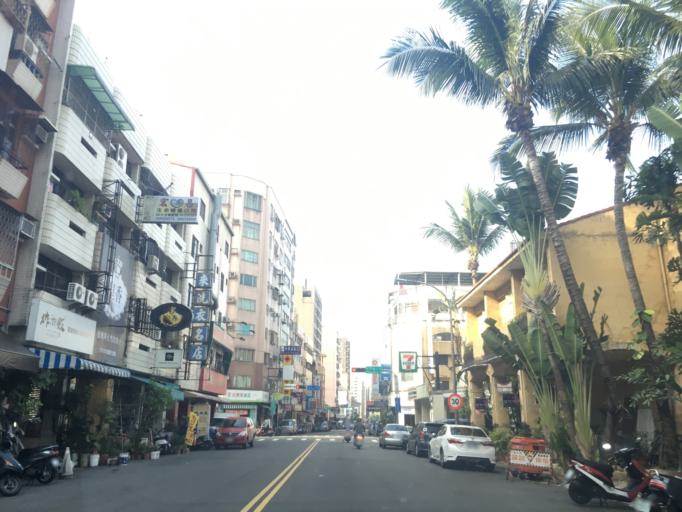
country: TW
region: Taiwan
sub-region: Taichung City
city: Taichung
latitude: 24.1716
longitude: 120.6816
